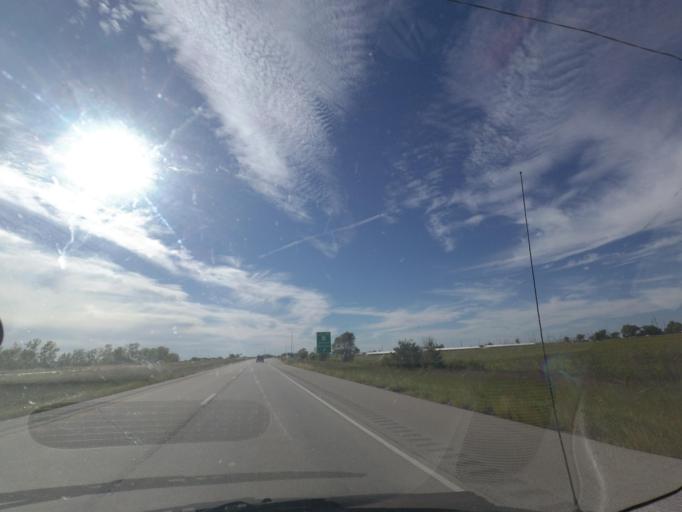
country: US
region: Illinois
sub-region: Macon County
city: Forsyth
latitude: 39.9108
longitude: -88.8840
